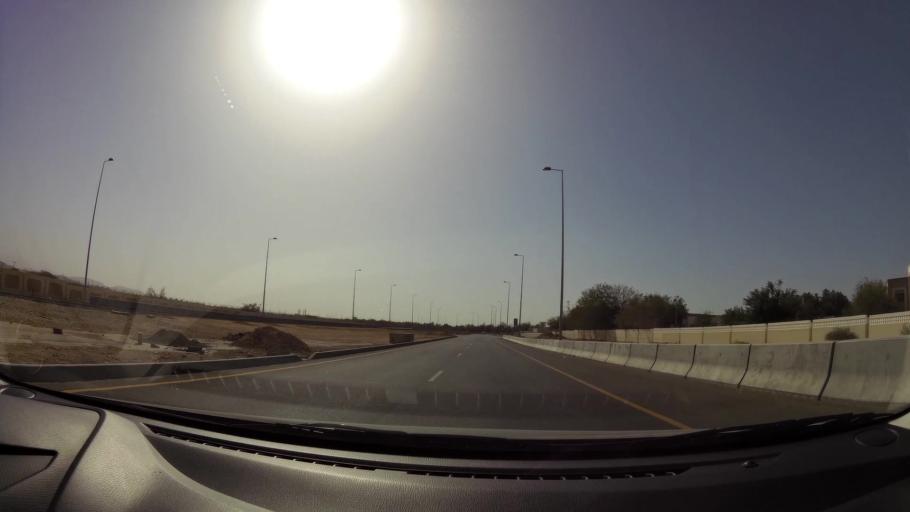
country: OM
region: Muhafazat Masqat
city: As Sib al Jadidah
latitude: 23.5794
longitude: 58.2744
